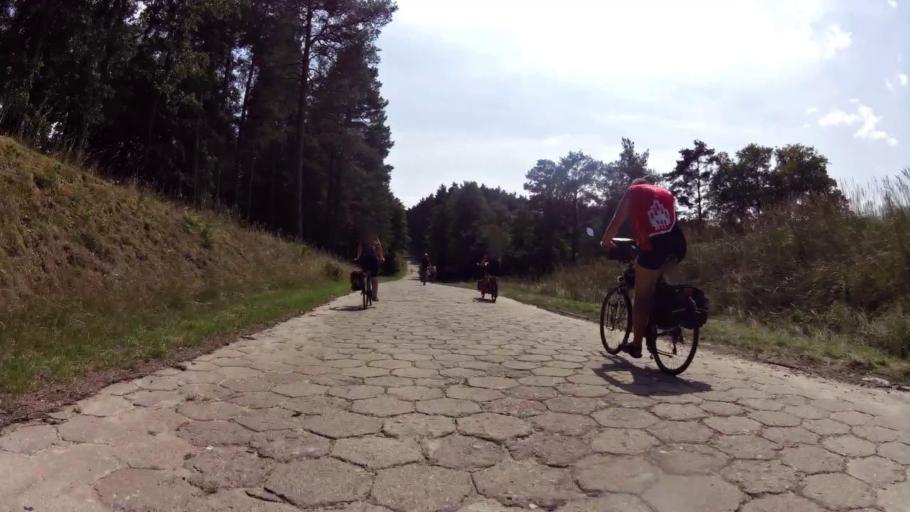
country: PL
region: West Pomeranian Voivodeship
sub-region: Powiat choszczenski
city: Drawno
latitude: 53.3351
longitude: 15.6982
